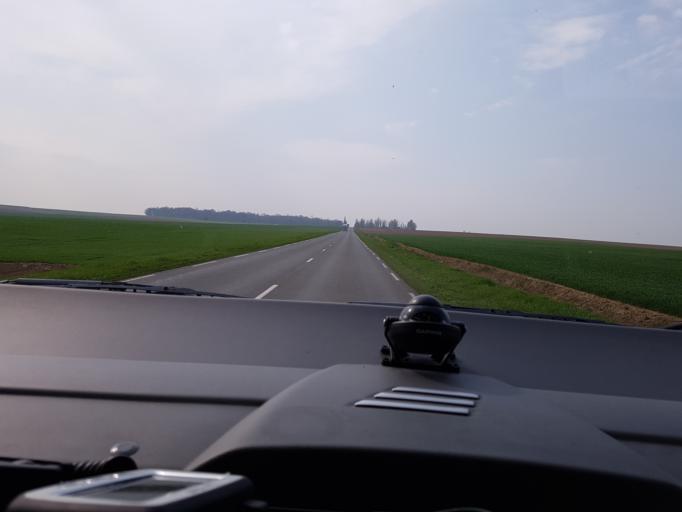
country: FR
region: Nord-Pas-de-Calais
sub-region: Departement du Nord
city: Masnieres
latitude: 50.0958
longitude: 3.2031
